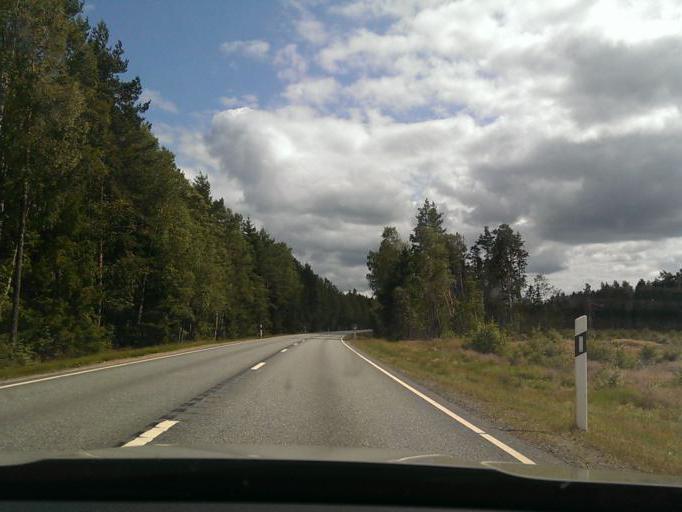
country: SE
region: Joenkoeping
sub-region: Varnamo Kommun
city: Varnamo
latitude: 57.2582
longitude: 13.9820
